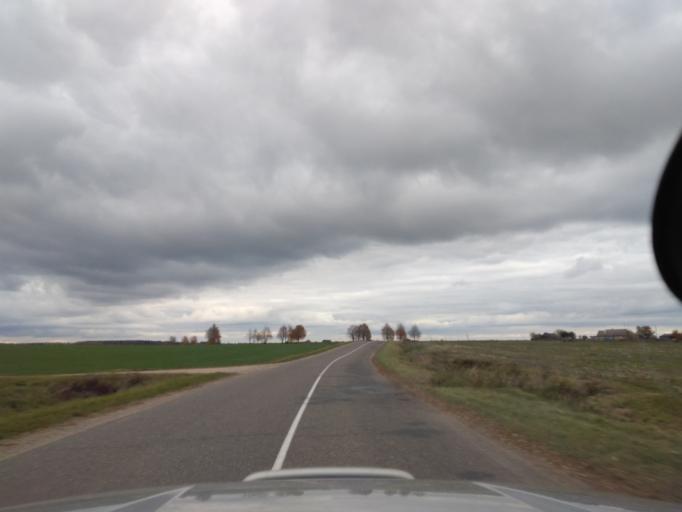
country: BY
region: Minsk
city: Slutsk
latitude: 53.2042
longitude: 27.3642
